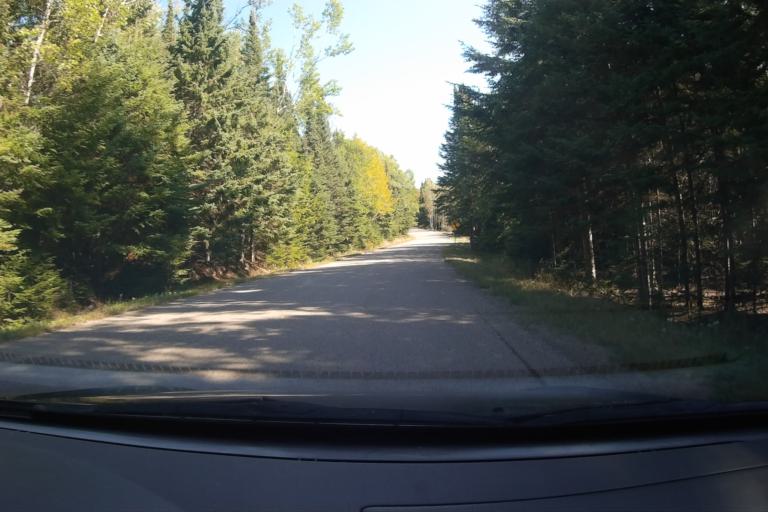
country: CA
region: Ontario
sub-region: Thunder Bay District
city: Thunder Bay
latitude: 48.3467
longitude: -88.8086
